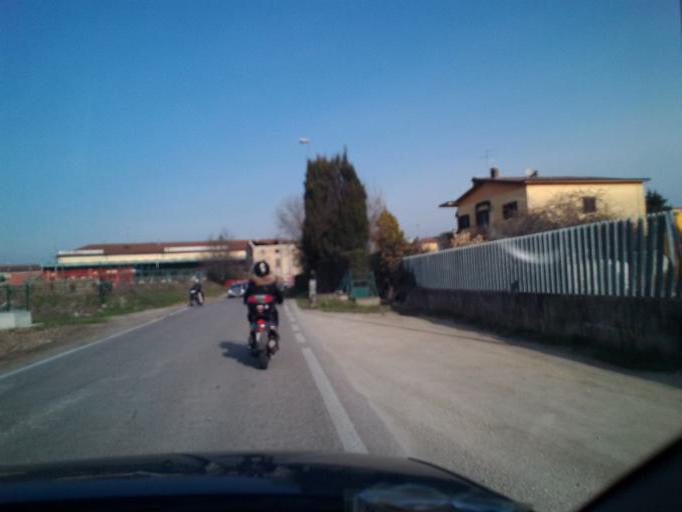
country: IT
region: Veneto
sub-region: Provincia di Verona
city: Villafranca di Verona
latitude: 45.3492
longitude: 10.8503
